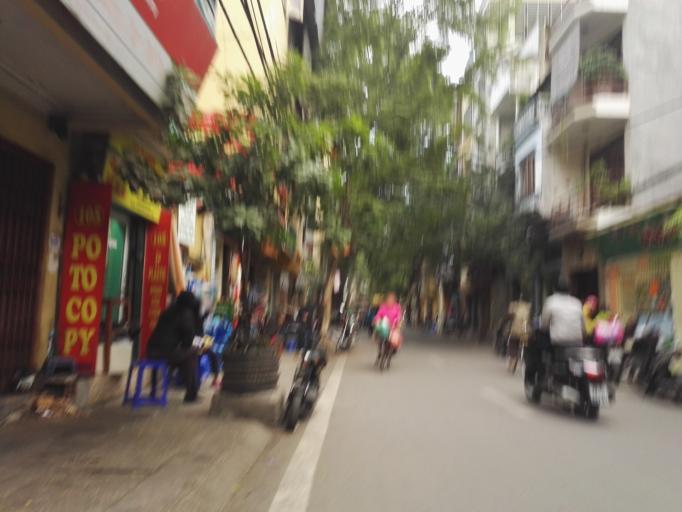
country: VN
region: Ha Noi
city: Hoan Kiem
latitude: 21.0469
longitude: 105.8486
